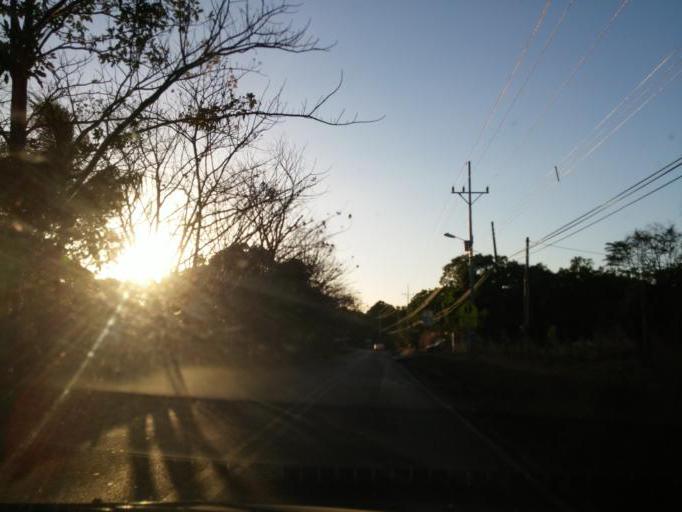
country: CR
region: Alajuela
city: Orotina
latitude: 9.9148
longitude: -84.5299
